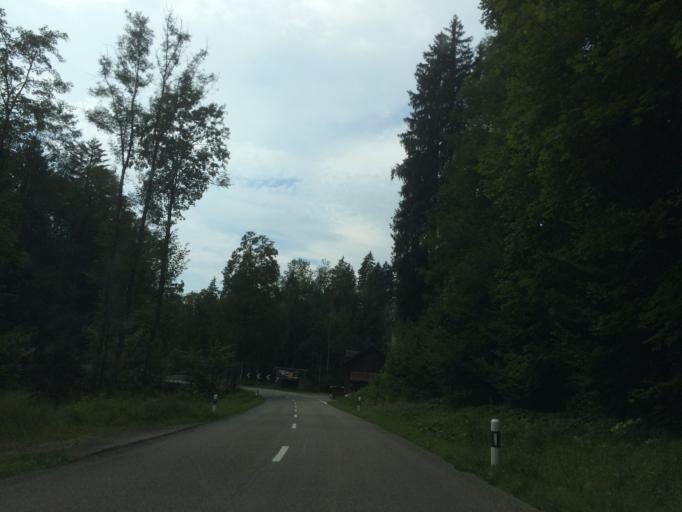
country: CH
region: Appenzell Ausserrhoden
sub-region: Bezirk Hinterland
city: Urnasch
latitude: 47.2453
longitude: 9.2600
